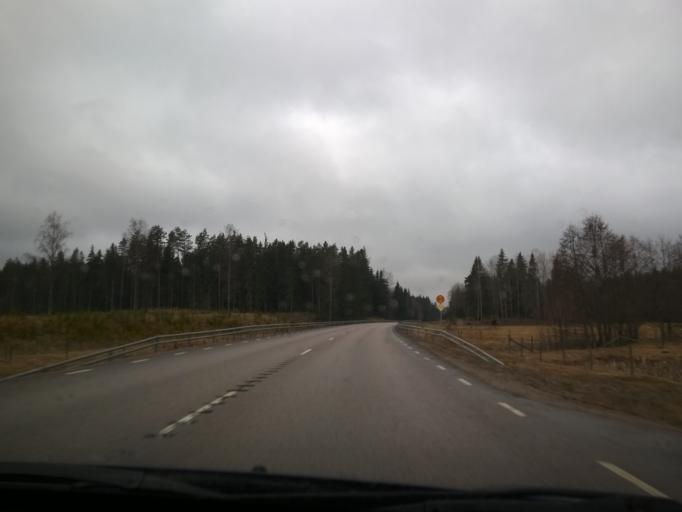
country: SE
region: Uppsala
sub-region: Osthammars Kommun
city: Bjorklinge
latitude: 60.1691
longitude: 17.5669
